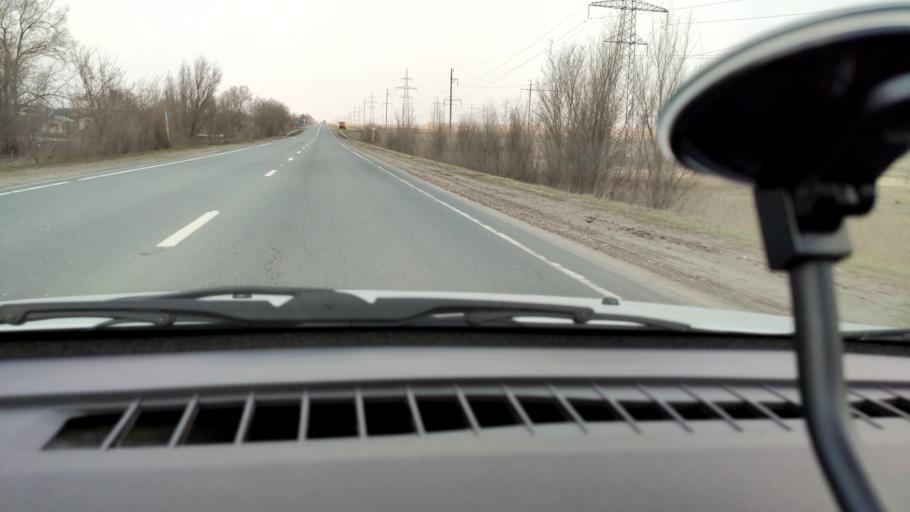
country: RU
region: Samara
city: Smyshlyayevka
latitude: 53.0882
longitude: 50.3953
